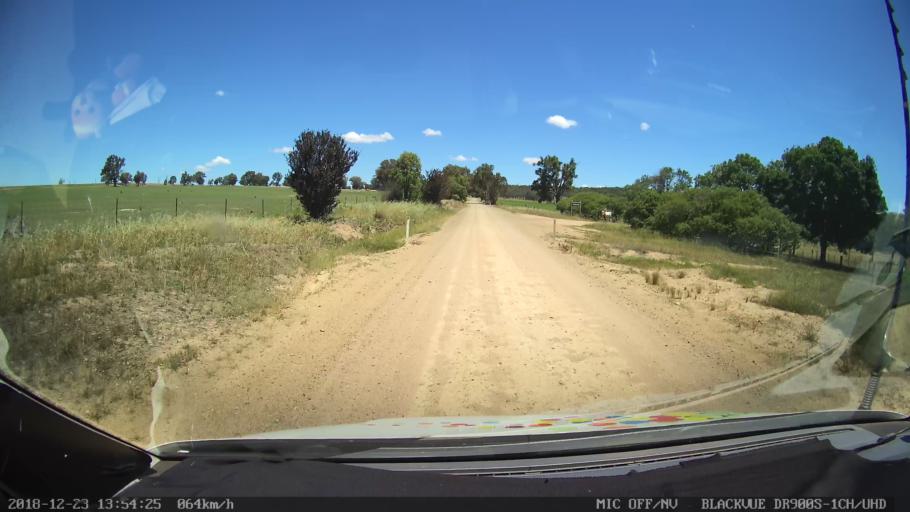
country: AU
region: New South Wales
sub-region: Tamworth Municipality
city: Manilla
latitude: -30.5608
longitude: 151.0907
